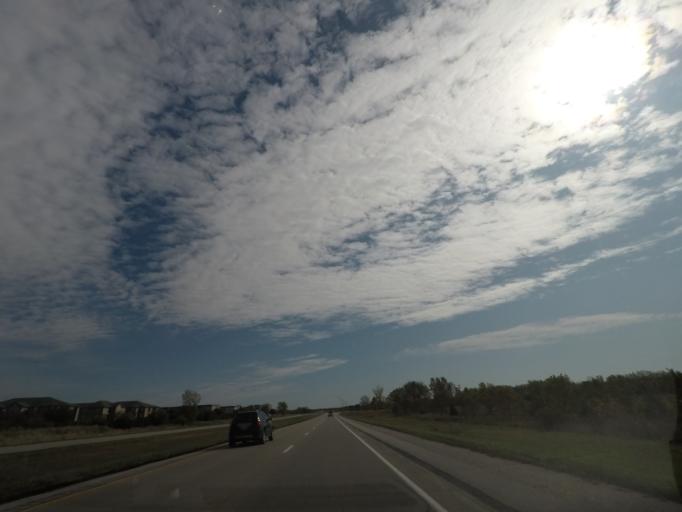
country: US
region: Iowa
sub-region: Story County
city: Ames
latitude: 42.0117
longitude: -93.6898
